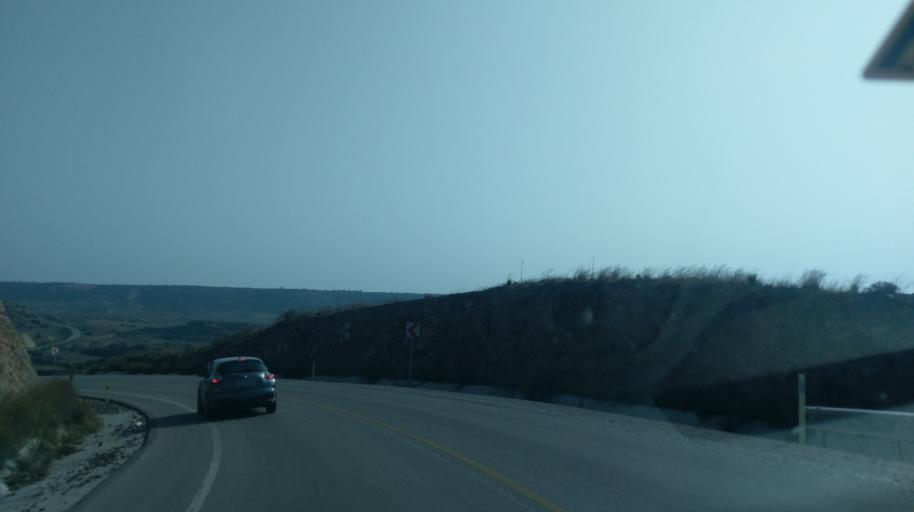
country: CY
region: Ammochostos
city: Leonarisso
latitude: 35.4801
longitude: 34.1070
